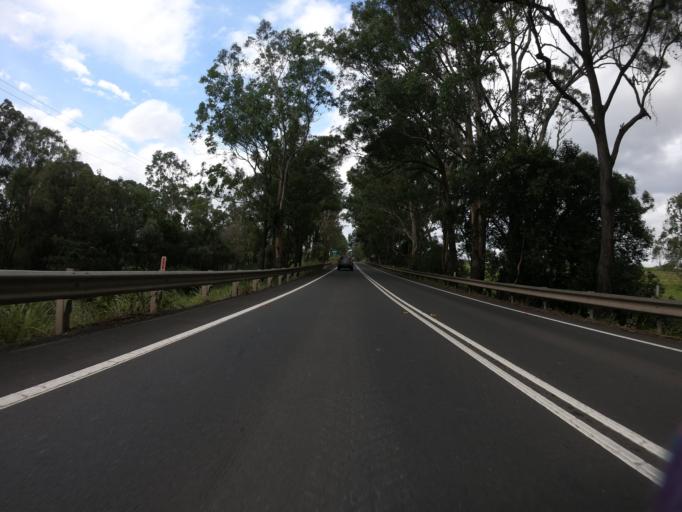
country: AU
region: New South Wales
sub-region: Blacktown
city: Riverstone
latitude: -33.6649
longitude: 150.8890
